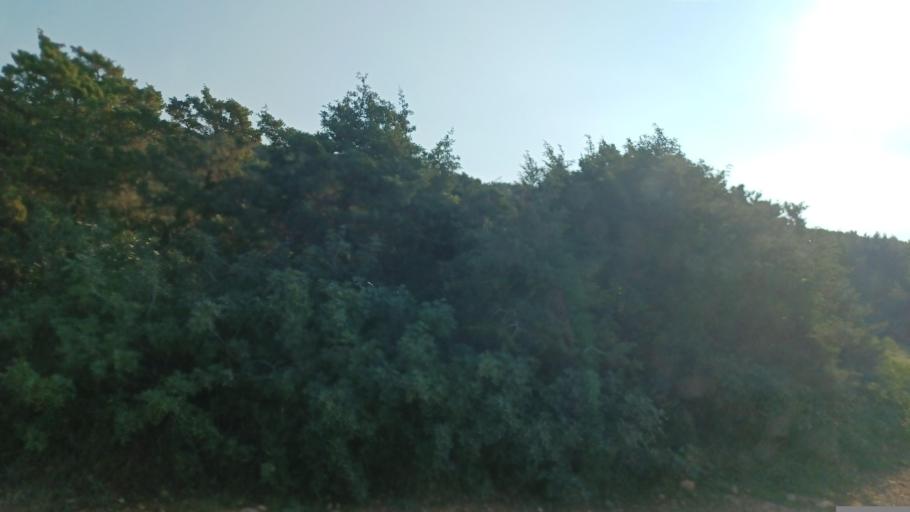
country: CY
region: Pafos
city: Pegeia
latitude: 34.9123
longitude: 32.3329
